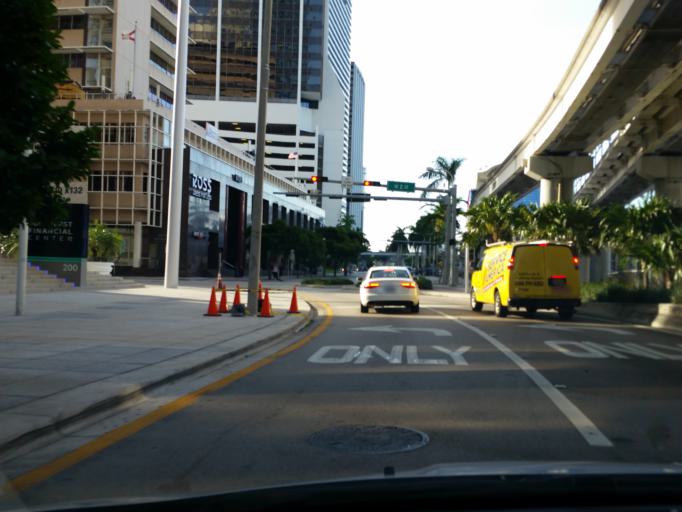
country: US
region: Florida
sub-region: Miami-Dade County
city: Miami
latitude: 25.7723
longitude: -80.1874
